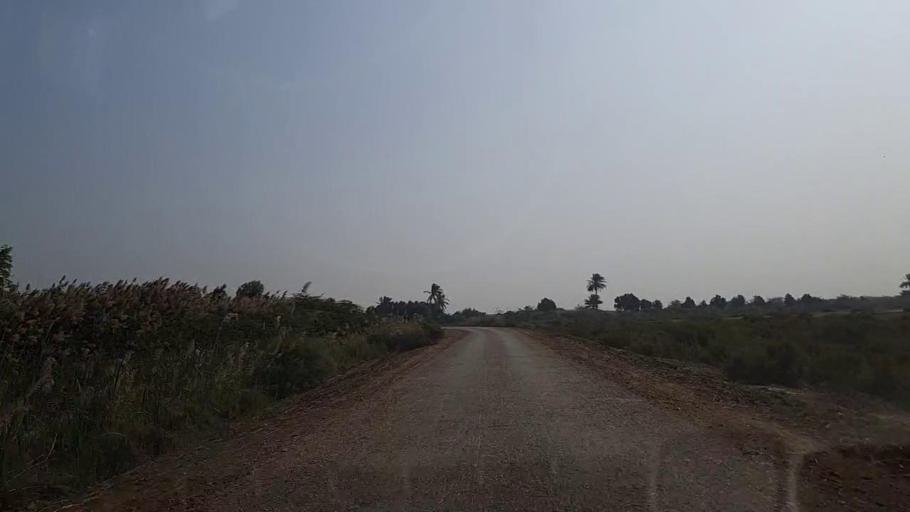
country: PK
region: Sindh
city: Keti Bandar
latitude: 24.2367
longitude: 67.6405
